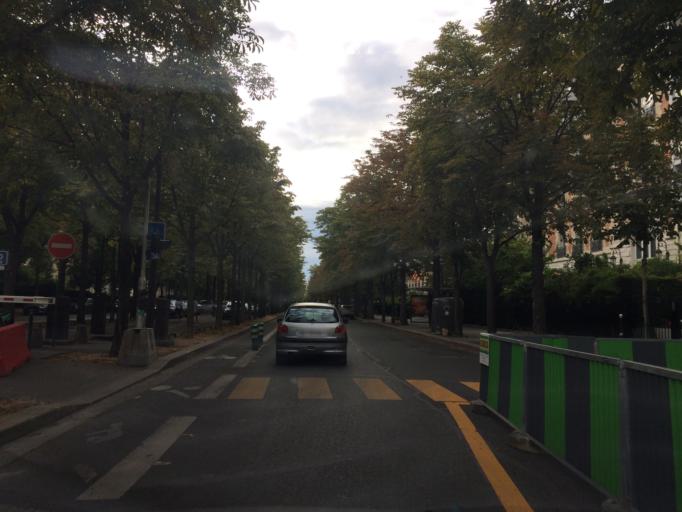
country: FR
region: Ile-de-France
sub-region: Departement des Hauts-de-Seine
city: Neuilly-sur-Seine
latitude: 48.8637
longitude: 2.2816
